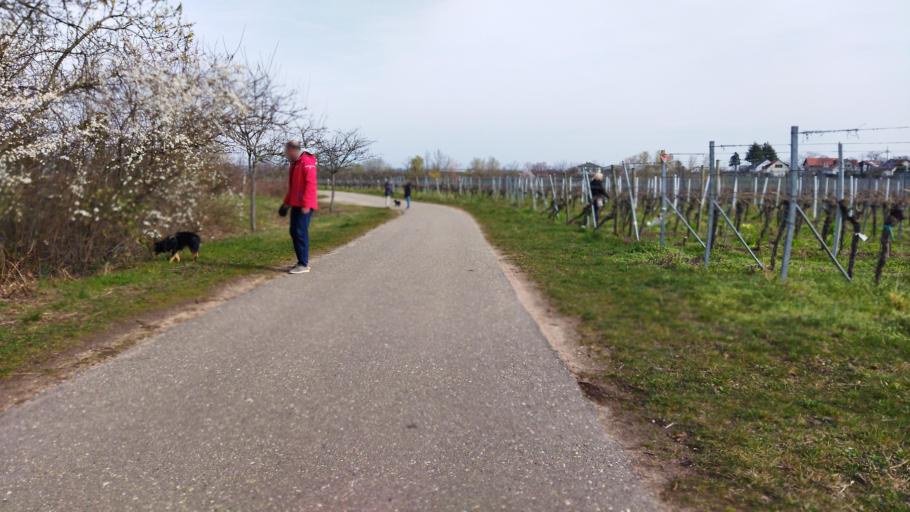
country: DE
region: Rheinland-Pfalz
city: Neustadt
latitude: 49.3749
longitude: 8.1647
